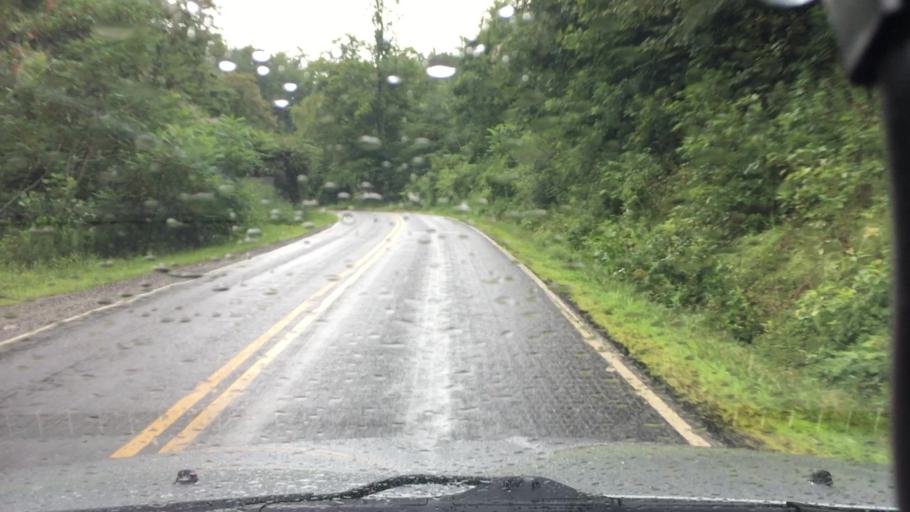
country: US
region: North Carolina
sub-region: Madison County
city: Mars Hill
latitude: 35.9122
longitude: -82.4896
